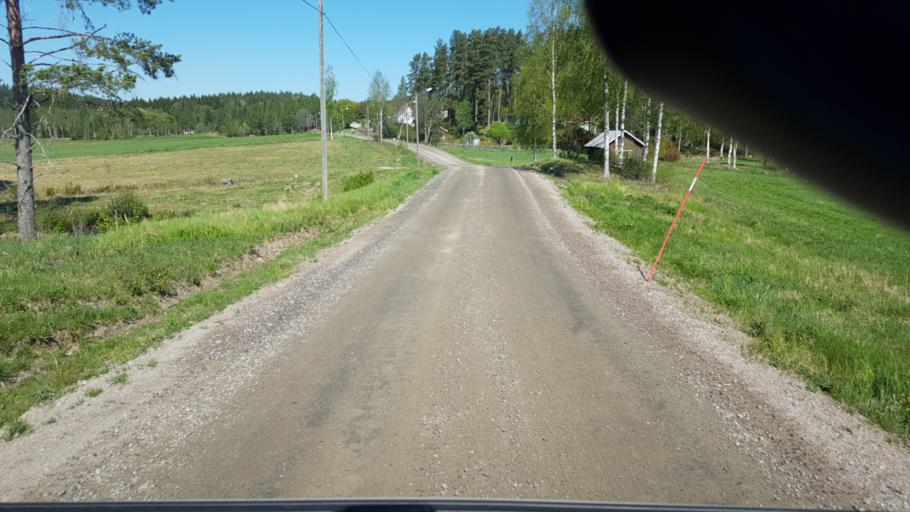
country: SE
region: Vaermland
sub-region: Arvika Kommun
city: Arvika
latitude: 59.8707
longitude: 12.6150
